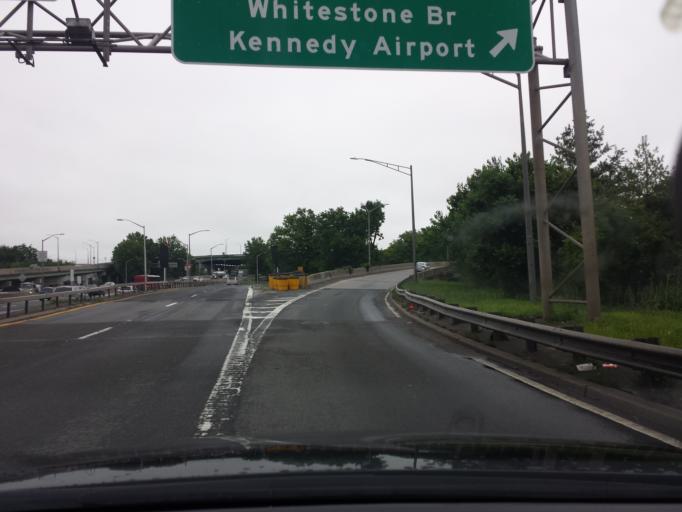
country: US
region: New York
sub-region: Queens County
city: Borough of Queens
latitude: 40.7418
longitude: -73.8410
